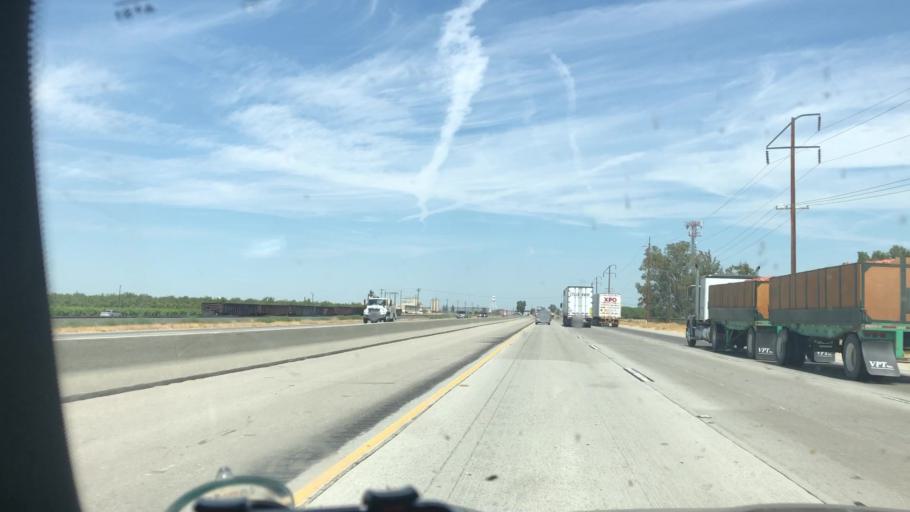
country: US
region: California
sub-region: Kern County
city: Rosedale
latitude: 35.4884
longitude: -119.1494
